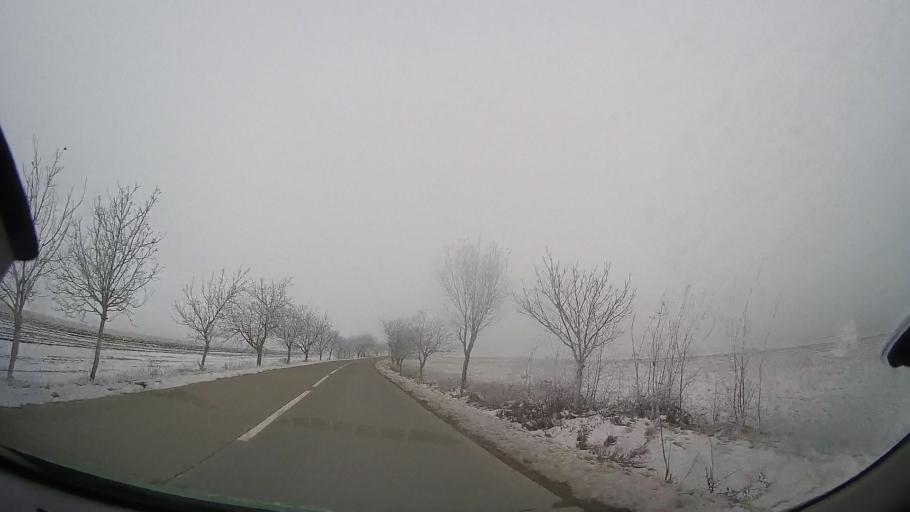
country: RO
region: Vaslui
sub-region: Comuna Ivesti
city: Ivesti
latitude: 46.1929
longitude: 27.5704
